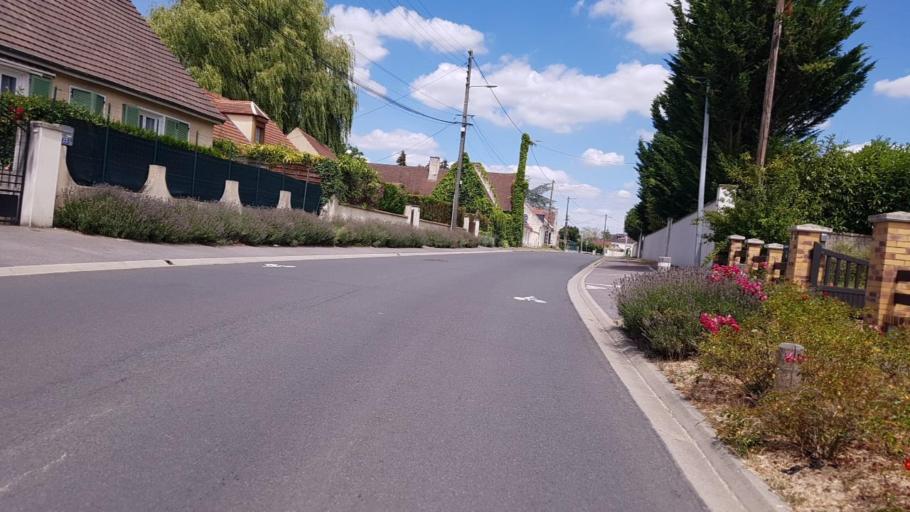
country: FR
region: Picardie
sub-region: Departement de l'Oise
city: Montmacq
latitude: 49.4826
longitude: 2.9550
